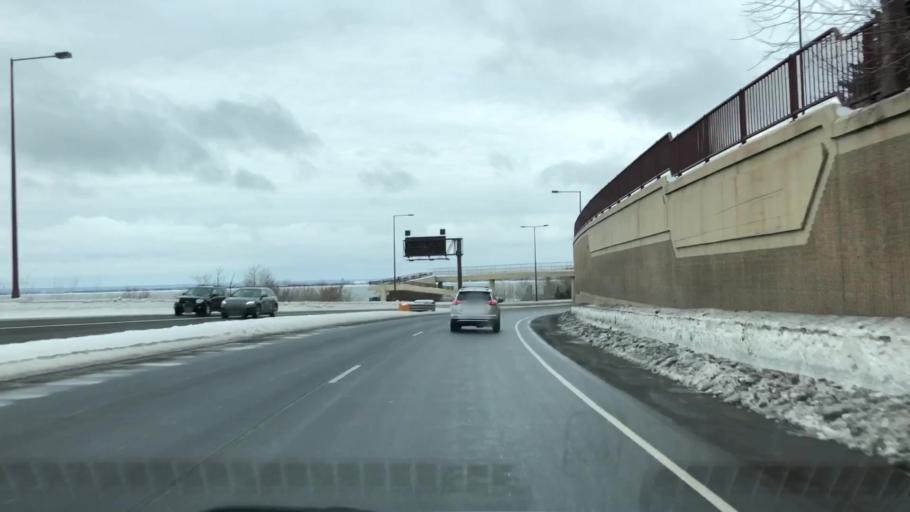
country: US
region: Minnesota
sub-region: Saint Louis County
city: Duluth
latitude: 46.8080
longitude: -92.0614
